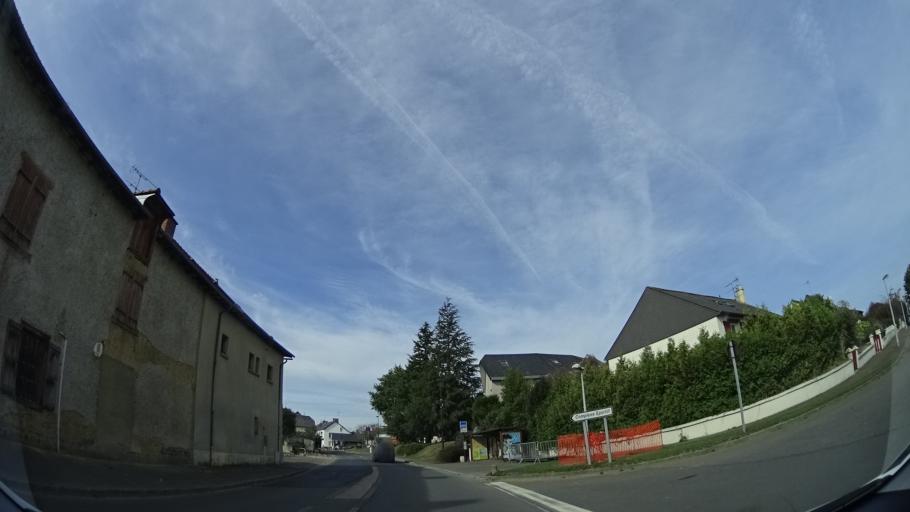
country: FR
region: Brittany
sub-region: Departement d'Ille-et-Vilaine
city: La Meziere
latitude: 48.2189
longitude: -1.7527
